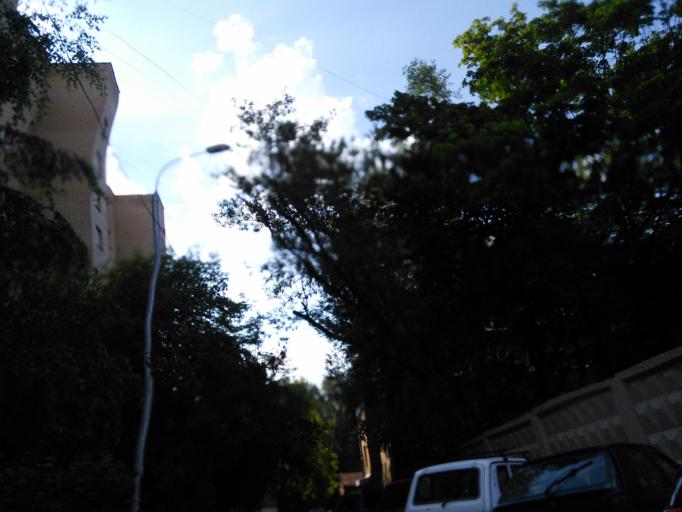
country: RU
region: Moskovskaya
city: Bogorodskoye
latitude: 55.8154
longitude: 37.7100
